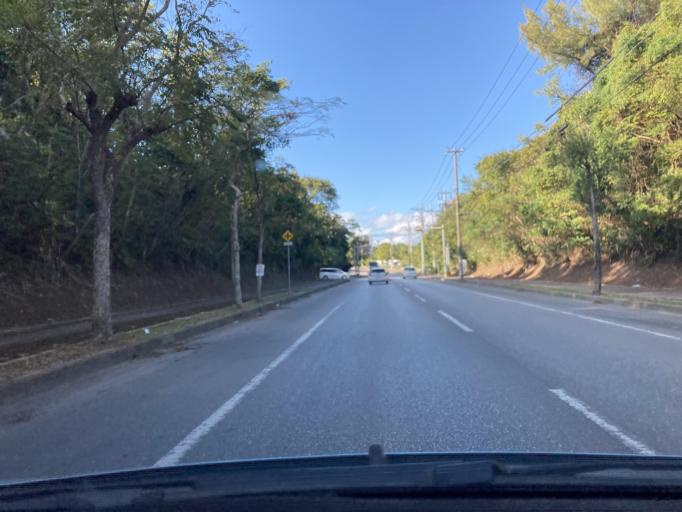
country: JP
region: Okinawa
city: Gushikawa
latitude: 26.3711
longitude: 127.8292
